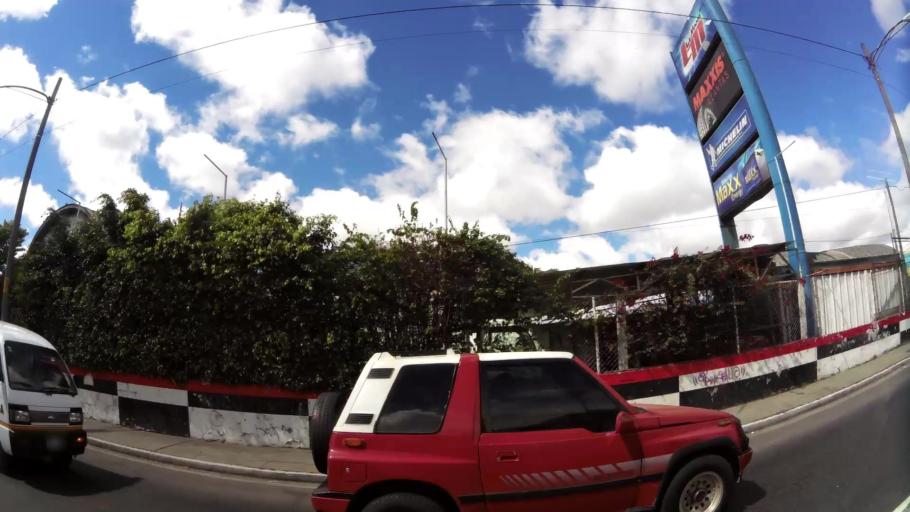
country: GT
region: Guatemala
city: Guatemala City
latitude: 14.5984
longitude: -90.5426
